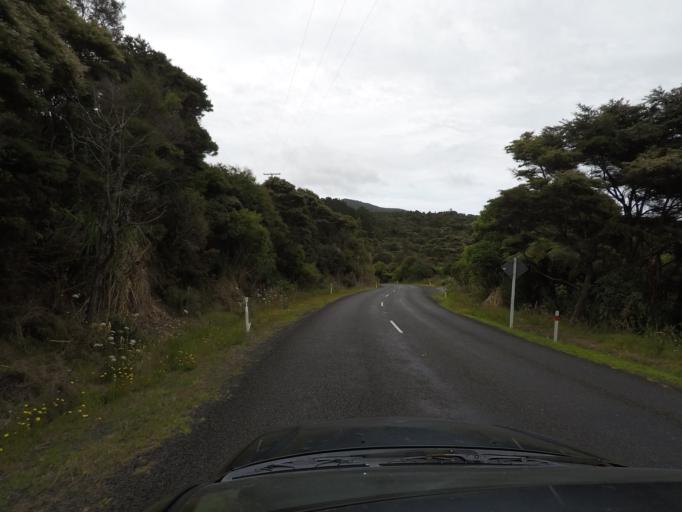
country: NZ
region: Waikato
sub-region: Waikato District
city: Raglan
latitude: -37.8253
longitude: 174.8189
